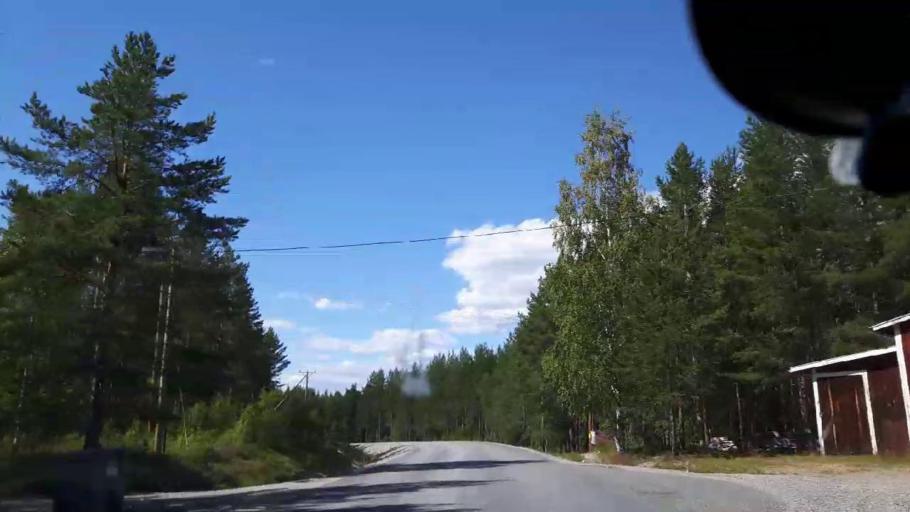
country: SE
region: Vaesternorrland
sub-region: Ange Kommun
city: Fransta
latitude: 62.6996
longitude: 16.3901
